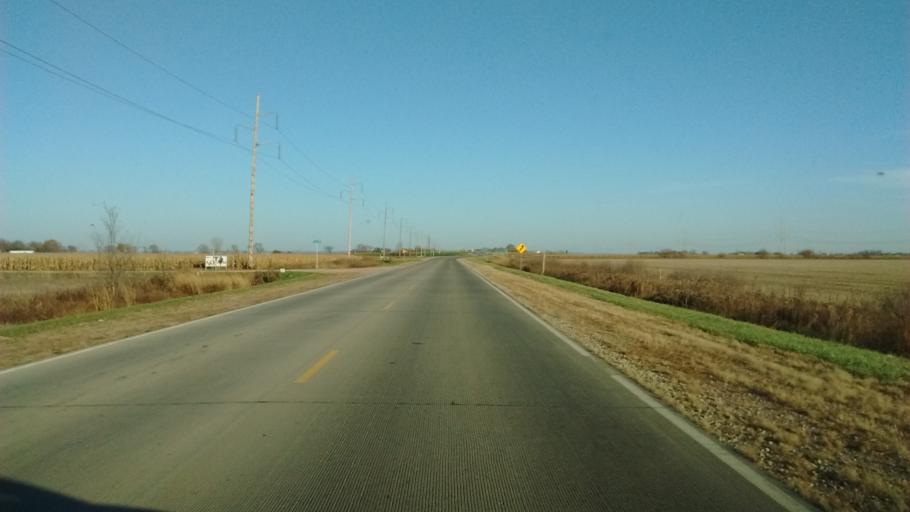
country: US
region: Iowa
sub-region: Woodbury County
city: Sergeant Bluff
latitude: 42.3302
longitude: -96.3309
